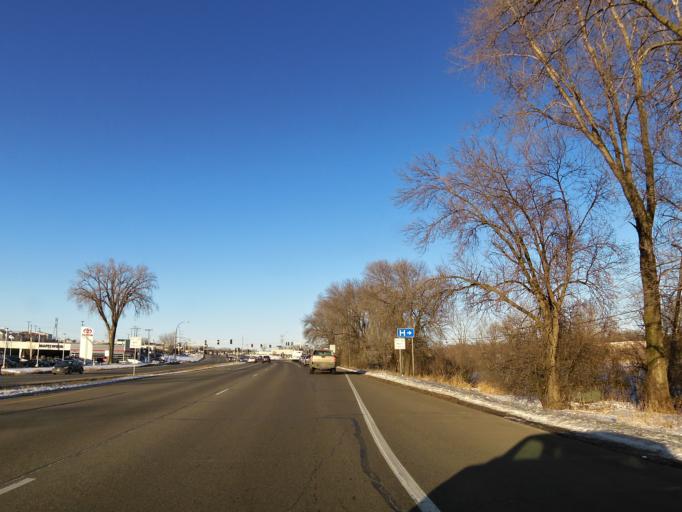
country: US
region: Minnesota
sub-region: Ramsey County
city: Little Canada
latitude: 45.0266
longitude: -93.0473
